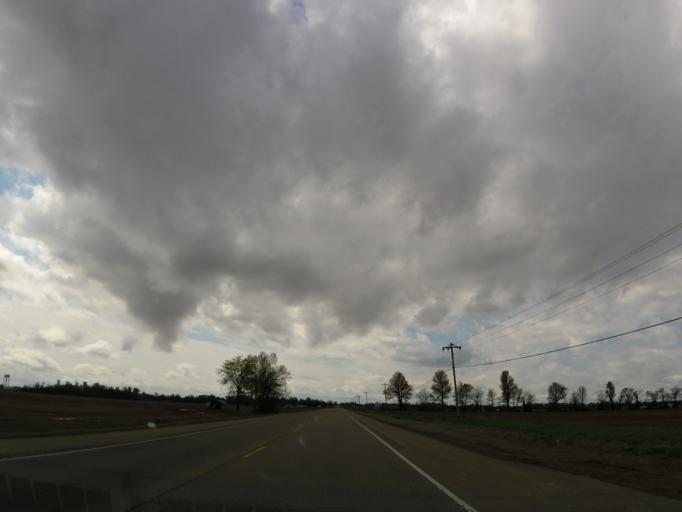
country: US
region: Arkansas
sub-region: Clay County
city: Corning
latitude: 36.4355
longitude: -90.5858
